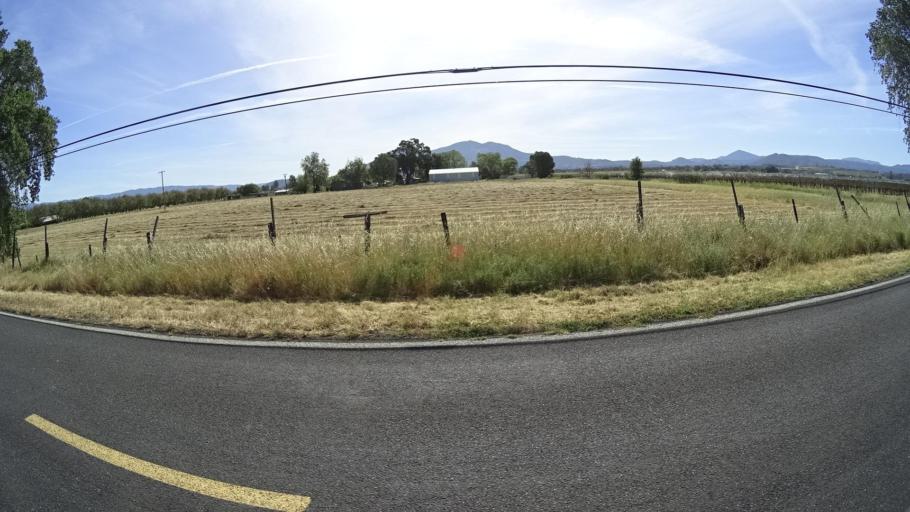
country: US
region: California
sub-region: Lake County
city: Kelseyville
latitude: 38.9780
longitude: -122.8946
